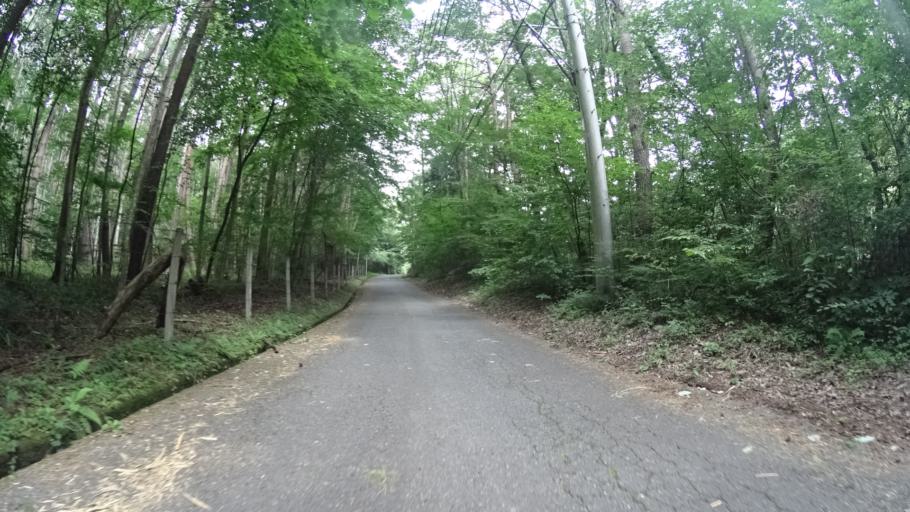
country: JP
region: Yamanashi
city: Nirasaki
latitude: 35.9066
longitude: 138.4221
